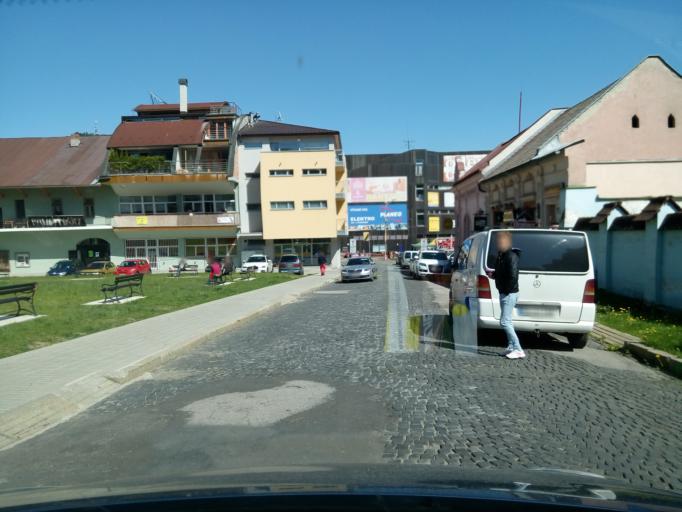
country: SK
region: Zilinsky
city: Ruzomberok
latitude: 49.0806
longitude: 19.3036
